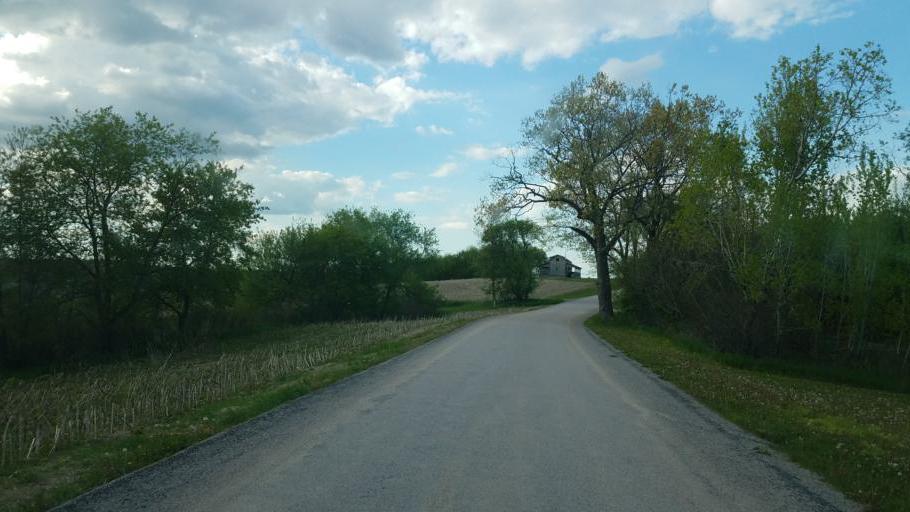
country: US
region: Wisconsin
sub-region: Vernon County
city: Hillsboro
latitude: 43.6507
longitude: -90.3735
